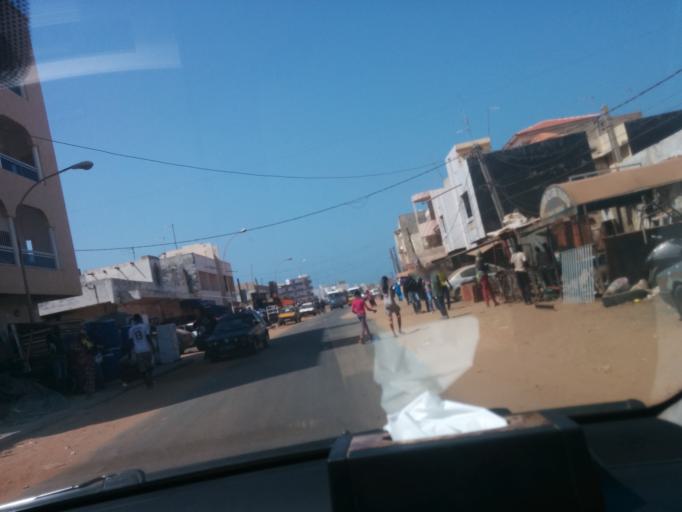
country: SN
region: Dakar
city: Pikine
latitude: 14.7707
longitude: -17.4241
